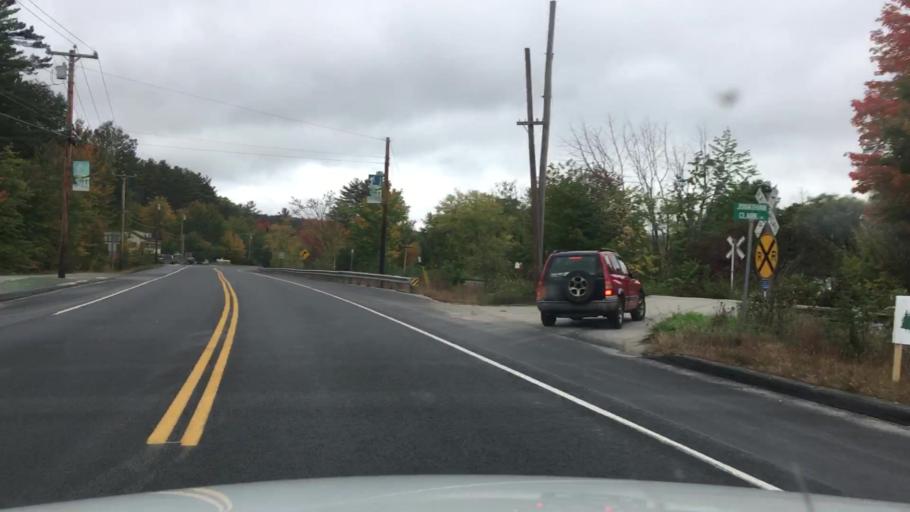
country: US
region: Maine
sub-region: Oxford County
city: Bethel
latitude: 44.4097
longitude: -70.8037
